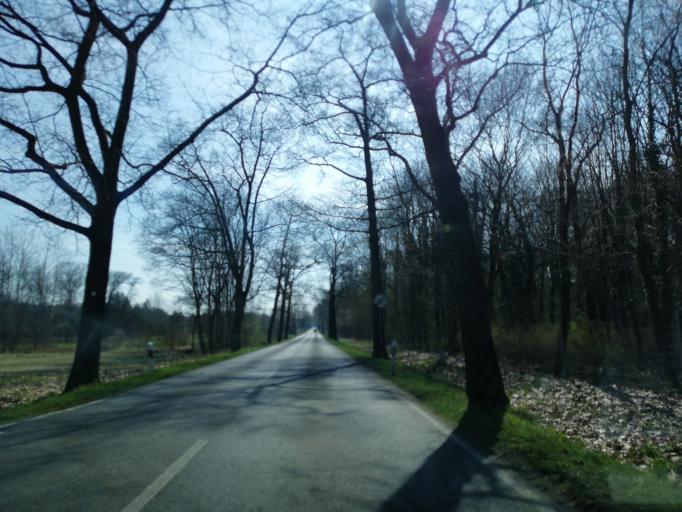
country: DE
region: Brandenburg
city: Altdobern
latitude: 51.6540
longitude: 14.0412
